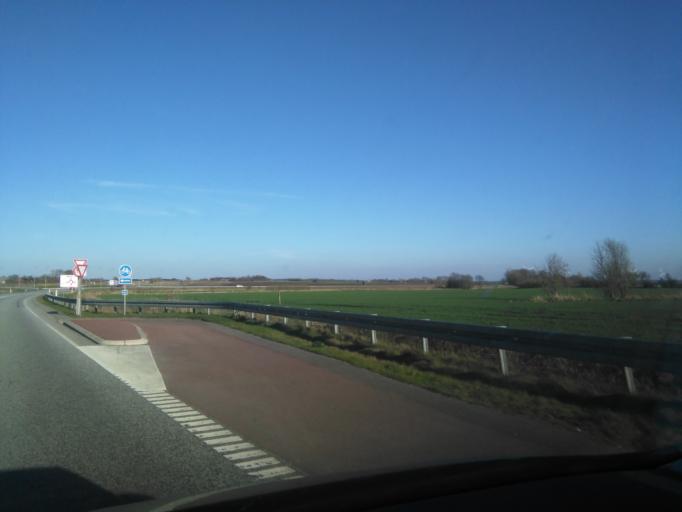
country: DK
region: Central Jutland
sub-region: Herning Kommune
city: Snejbjerg
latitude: 56.1281
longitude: 8.8685
